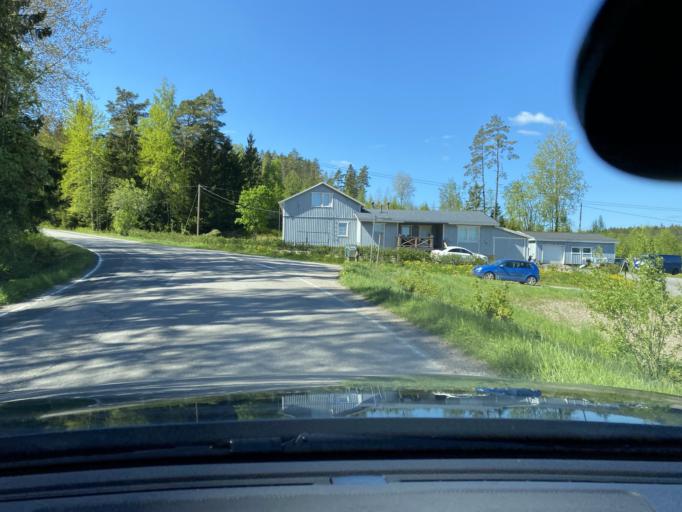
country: FI
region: Varsinais-Suomi
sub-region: Turku
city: Piikkioe
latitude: 60.4591
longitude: 22.5425
